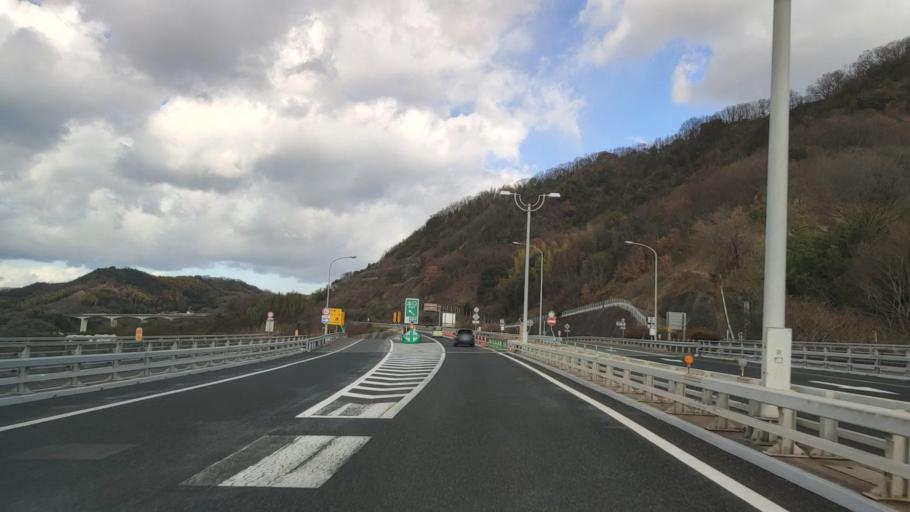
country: JP
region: Hiroshima
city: Innoshima
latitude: 34.3070
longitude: 133.1539
